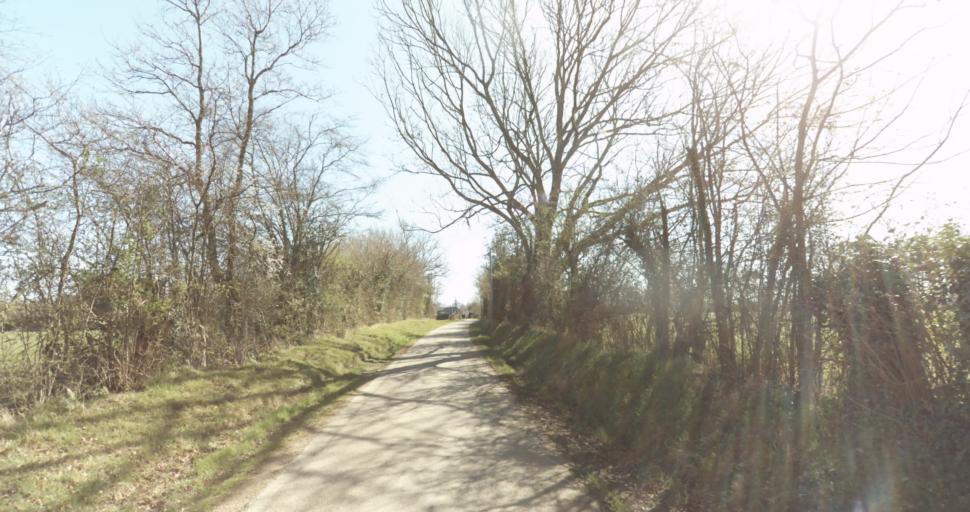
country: FR
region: Lower Normandy
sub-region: Departement du Calvados
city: Livarot
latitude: 48.9949
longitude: 0.0788
